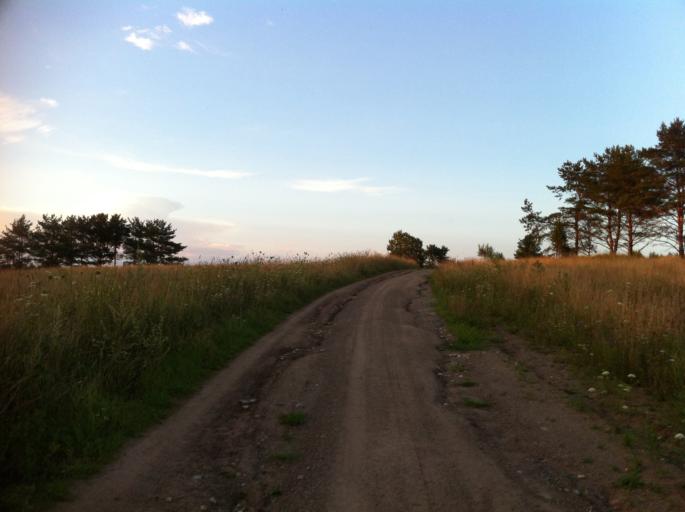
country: RU
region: Pskov
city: Izborsk
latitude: 57.8220
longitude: 27.9653
